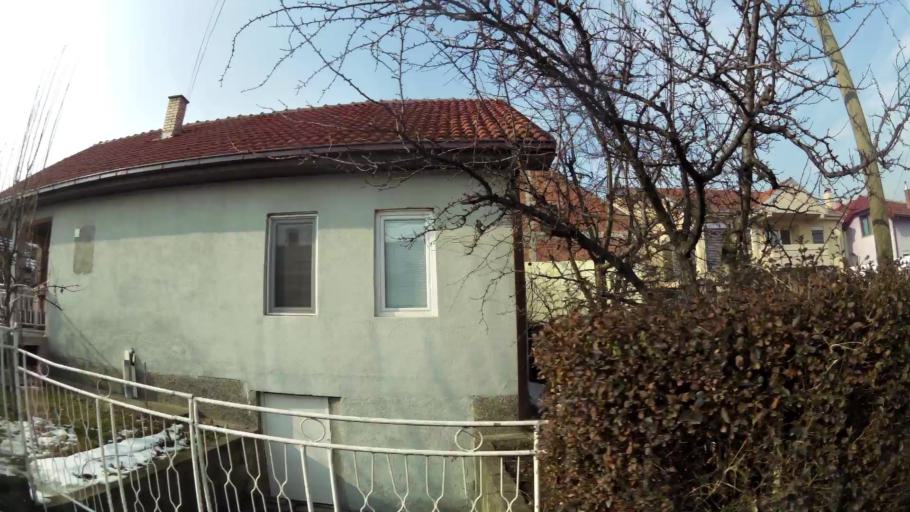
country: MK
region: Kisela Voda
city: Kisela Voda
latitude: 41.9908
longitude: 21.4977
